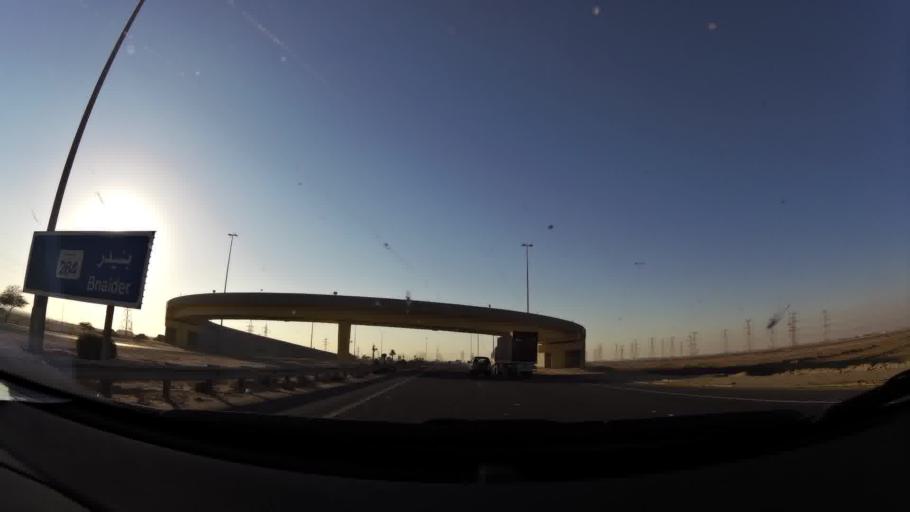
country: KW
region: Al Ahmadi
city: Al Fahahil
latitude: 28.7793
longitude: 48.2755
